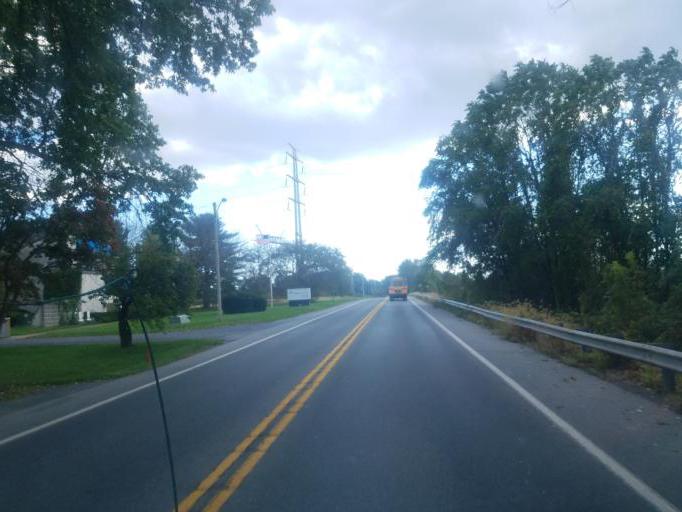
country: US
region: Pennsylvania
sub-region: Dauphin County
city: Middletown
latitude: 40.1536
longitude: -76.7174
